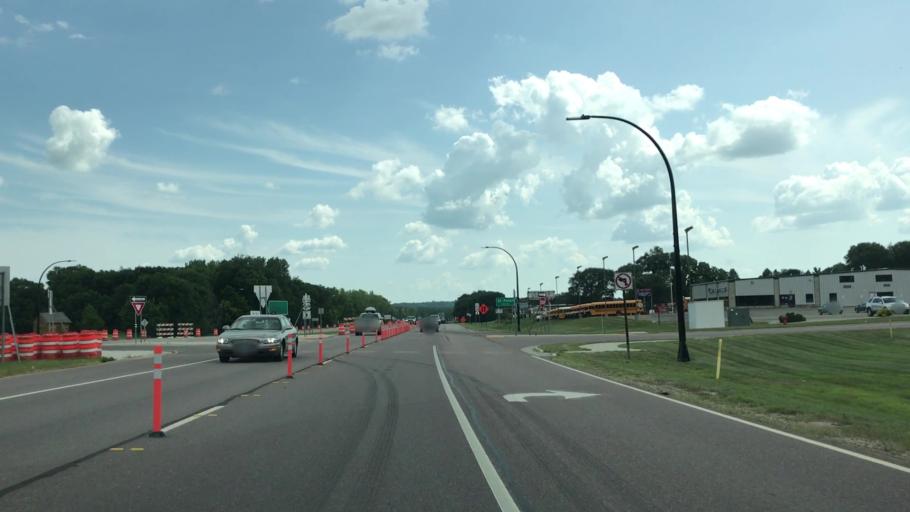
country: US
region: Minnesota
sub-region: Nicollet County
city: Saint Peter
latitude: 44.3495
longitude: -93.9519
